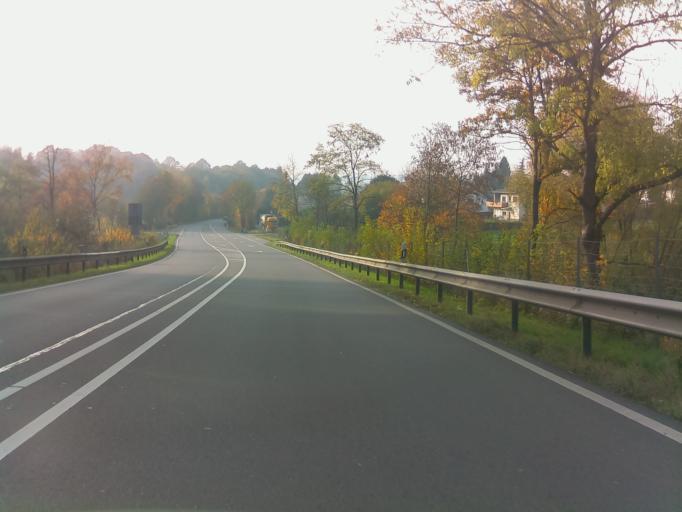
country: DE
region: Baden-Wuerttemberg
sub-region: Karlsruhe Region
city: Aglasterhausen
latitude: 49.3516
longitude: 9.0063
